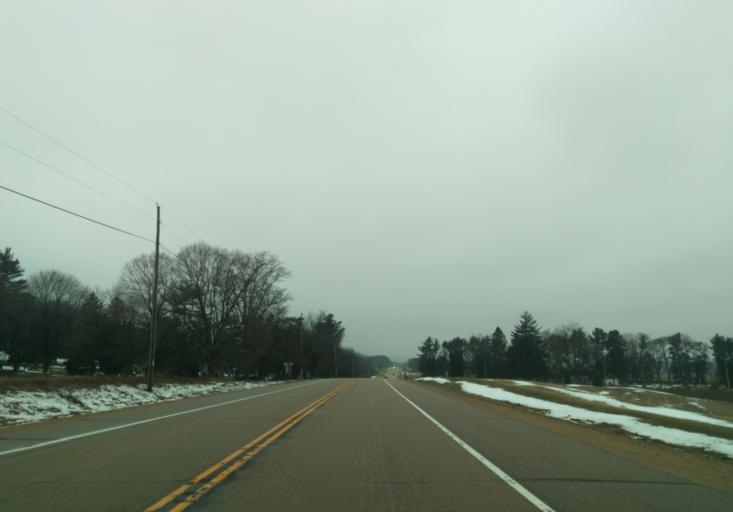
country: US
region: Wisconsin
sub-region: Dane County
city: Mazomanie
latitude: 43.1680
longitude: -89.8114
